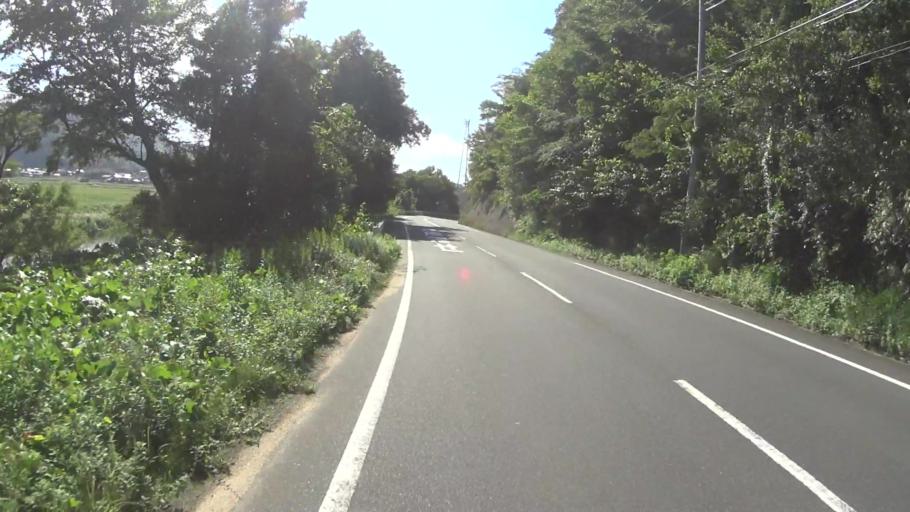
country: JP
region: Kyoto
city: Miyazu
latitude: 35.6483
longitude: 135.0847
